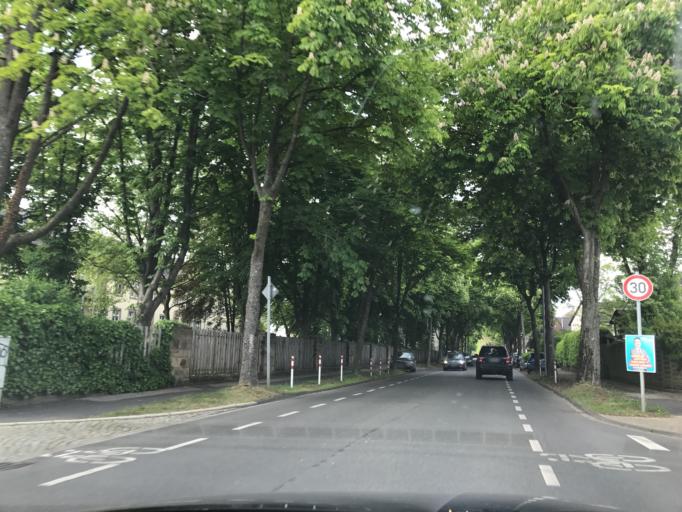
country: DE
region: North Rhine-Westphalia
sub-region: Regierungsbezirk Dusseldorf
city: Muelheim (Ruhr)
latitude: 51.4137
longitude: 6.9077
